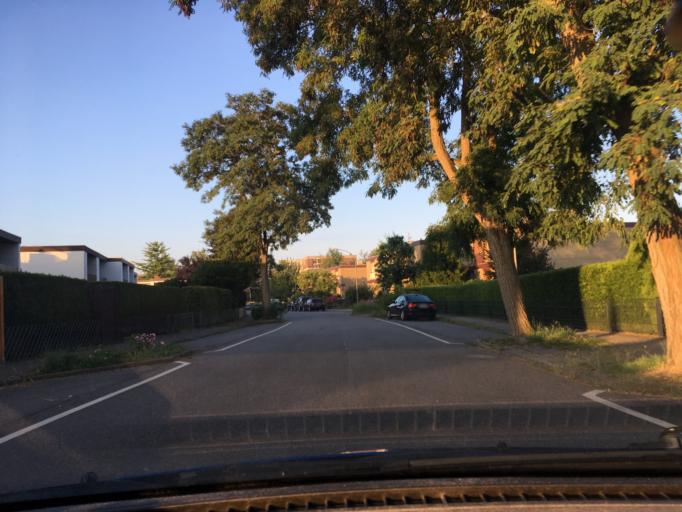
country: DE
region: Lower Saxony
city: Seevetal
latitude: 53.3853
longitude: 9.9876
